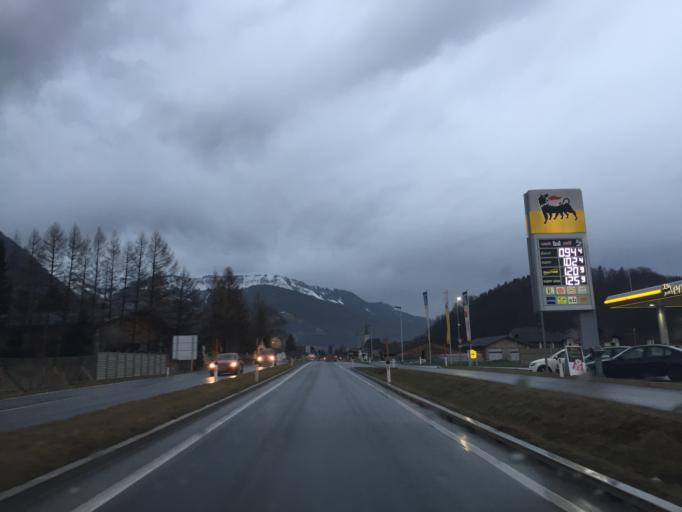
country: AT
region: Salzburg
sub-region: Politischer Bezirk Hallein
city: Golling an der Salzach
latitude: 47.5917
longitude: 13.1755
